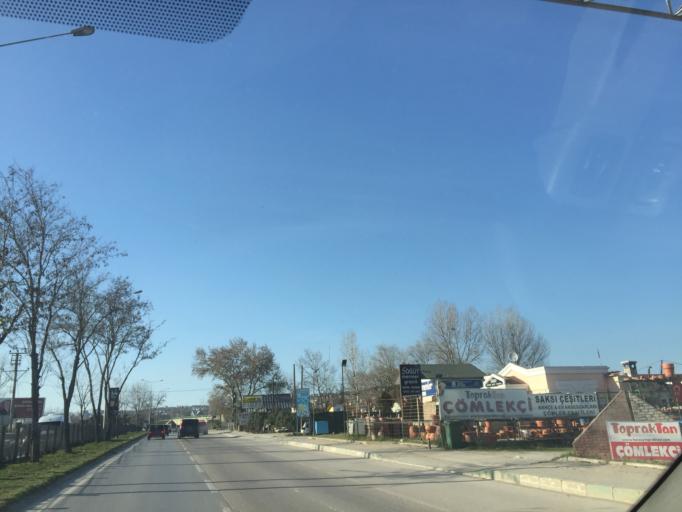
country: TR
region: Bursa
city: Niluefer
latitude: 40.2786
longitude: 28.9372
